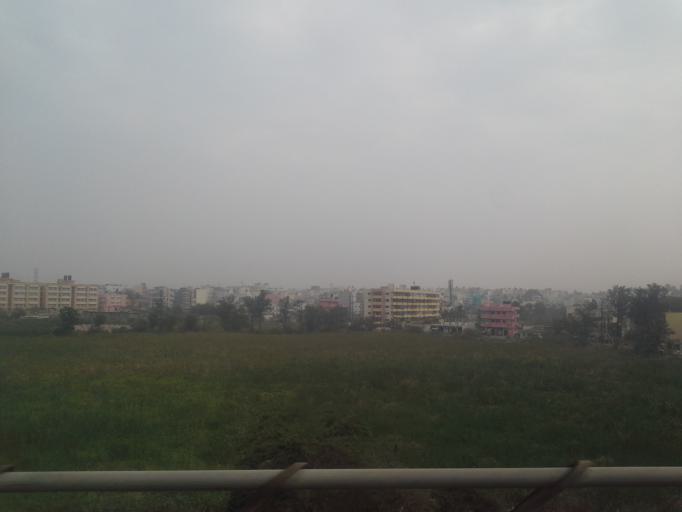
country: IN
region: Karnataka
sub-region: Bangalore Urban
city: Bangalore
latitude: 12.8952
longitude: 77.6363
